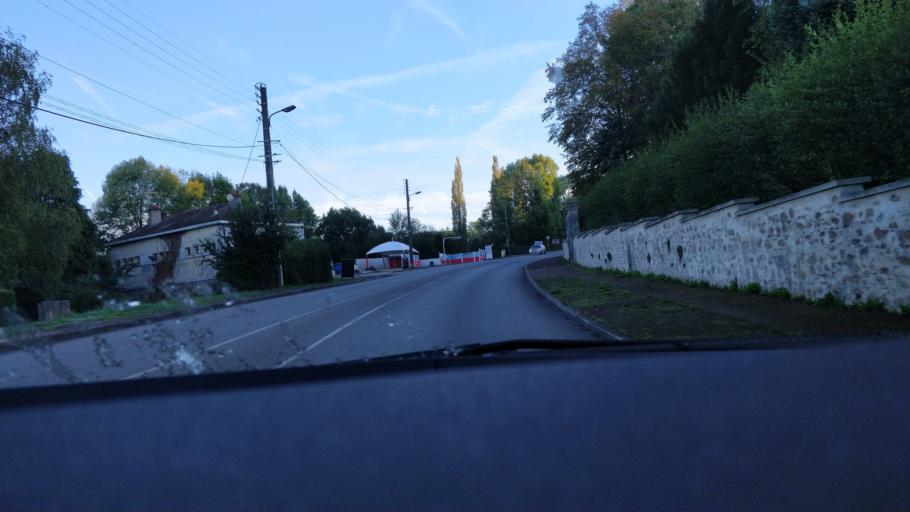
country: FR
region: Limousin
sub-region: Departement de la Haute-Vienne
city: Saint-Leonard-de-Noblat
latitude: 45.8333
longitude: 1.4873
